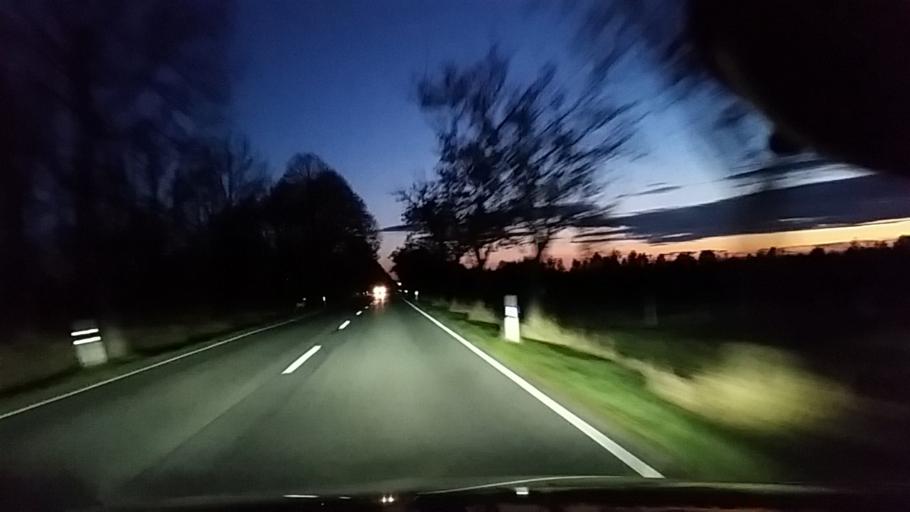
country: DE
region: Lower Saxony
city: Tappenbeck
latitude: 52.4618
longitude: 10.7581
